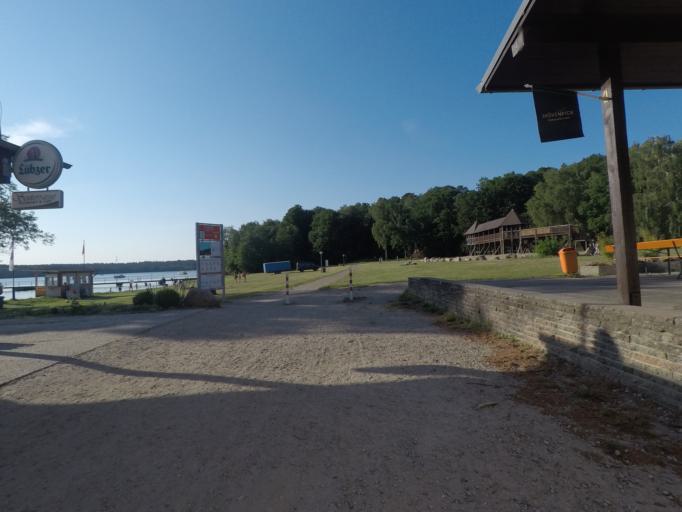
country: DE
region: Brandenburg
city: Joachimsthal
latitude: 52.9215
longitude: 13.7246
